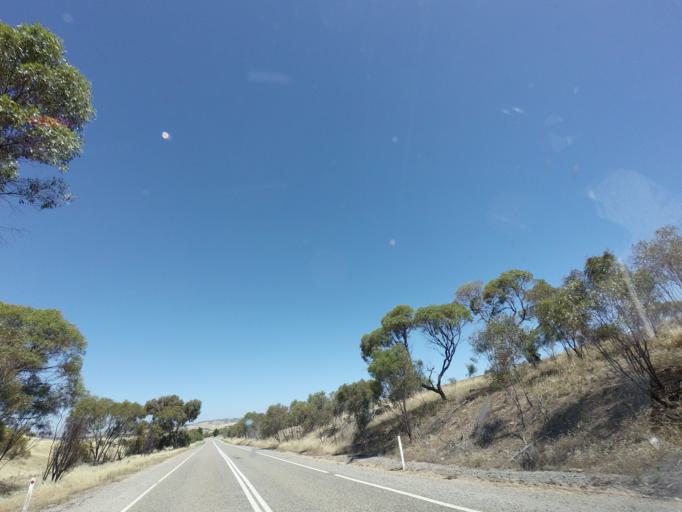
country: AU
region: South Australia
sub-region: Peterborough
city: Peterborough
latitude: -32.7440
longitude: 138.5552
